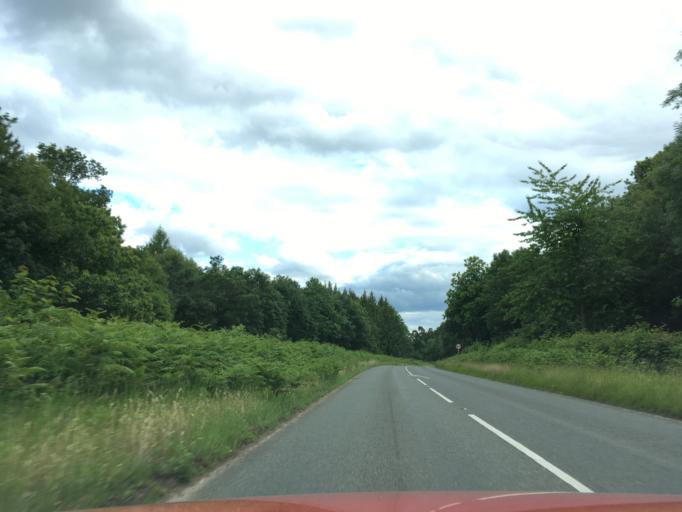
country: GB
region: England
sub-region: Oxfordshire
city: Boars Hill
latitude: 51.7128
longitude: -1.2654
